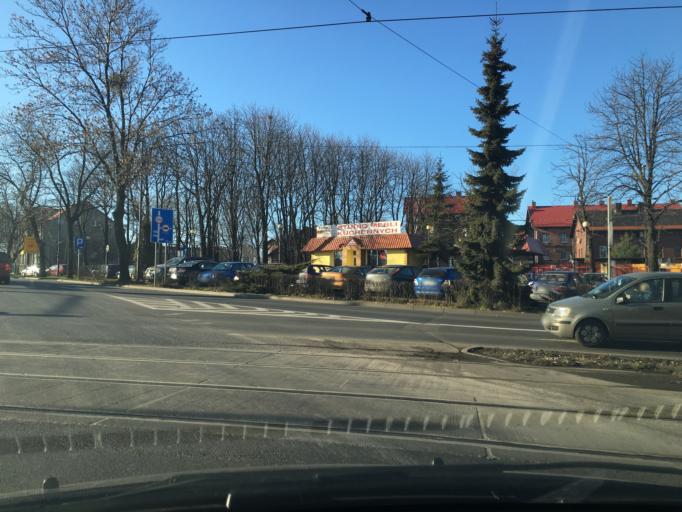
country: PL
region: Silesian Voivodeship
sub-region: Swietochlowice
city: Swietochlowice
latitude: 50.3018
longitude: 18.8832
